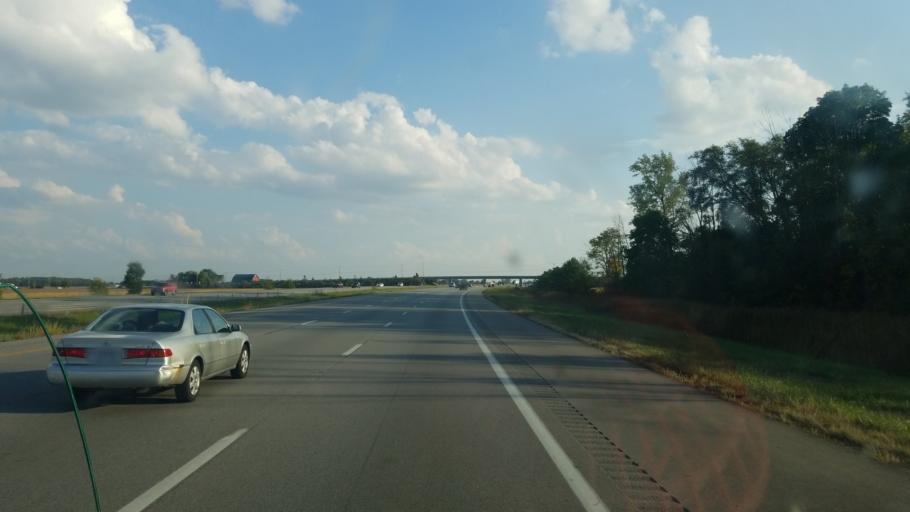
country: US
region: Ohio
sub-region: Wood County
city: Bowling Green
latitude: 41.4331
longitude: -83.6173
